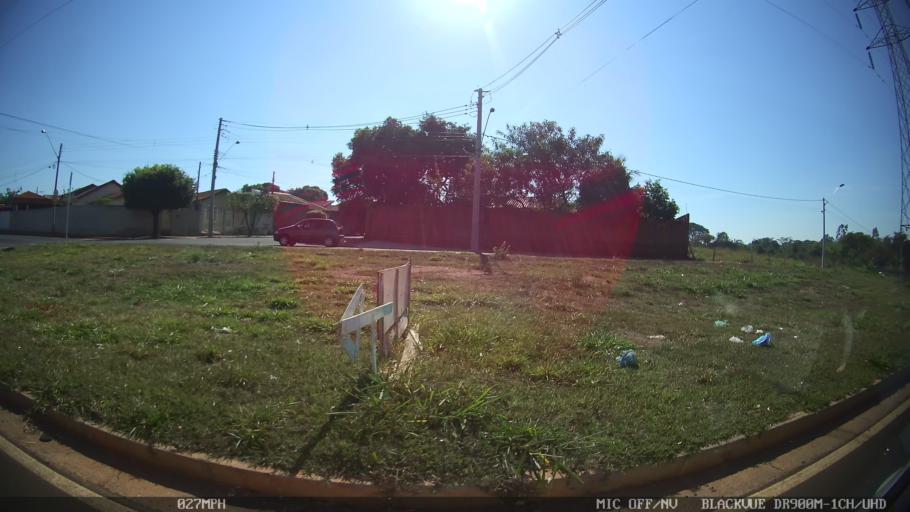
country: BR
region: Sao Paulo
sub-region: Sao Jose Do Rio Preto
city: Sao Jose do Rio Preto
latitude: -20.7643
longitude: -49.3614
